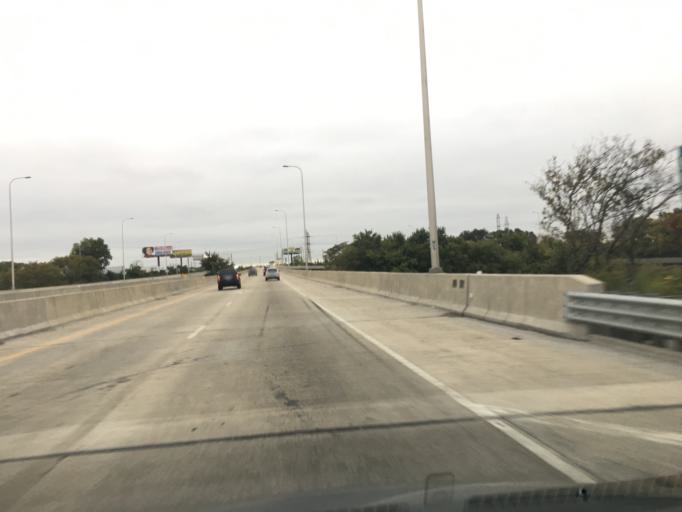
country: US
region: Illinois
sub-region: Cook County
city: Summit
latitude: 41.7943
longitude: -87.8227
